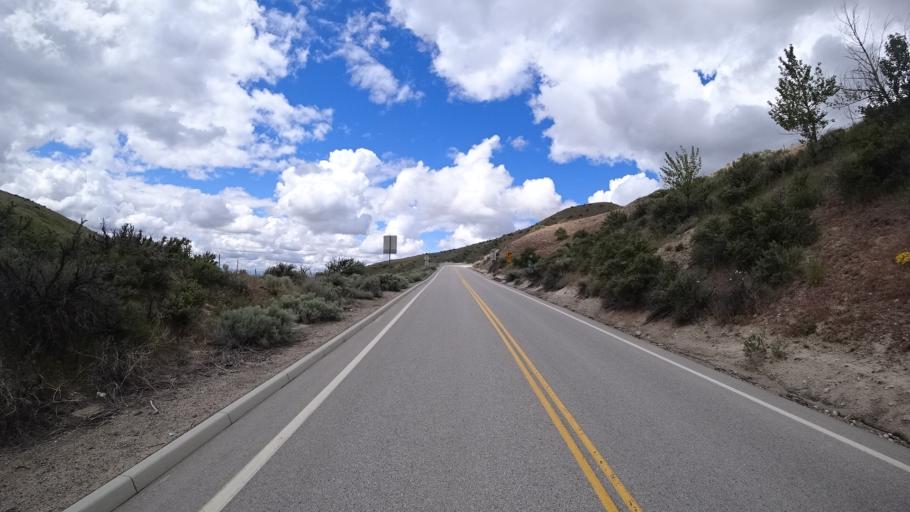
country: US
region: Idaho
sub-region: Ada County
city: Boise
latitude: 43.6827
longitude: -116.1801
